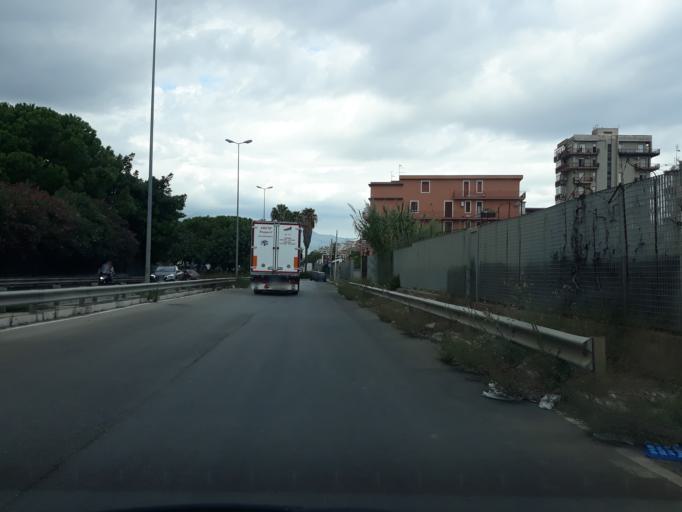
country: IT
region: Sicily
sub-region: Palermo
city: Ciaculli
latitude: 38.0935
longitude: 13.4045
